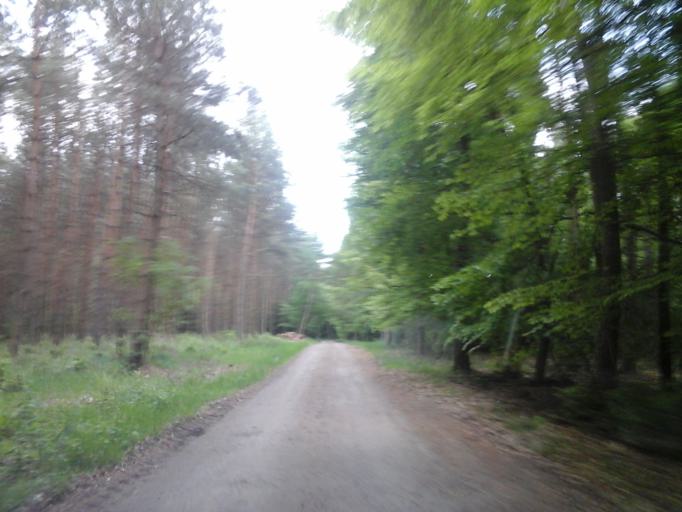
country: PL
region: West Pomeranian Voivodeship
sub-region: Powiat choszczenski
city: Pelczyce
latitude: 52.9524
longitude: 15.3354
